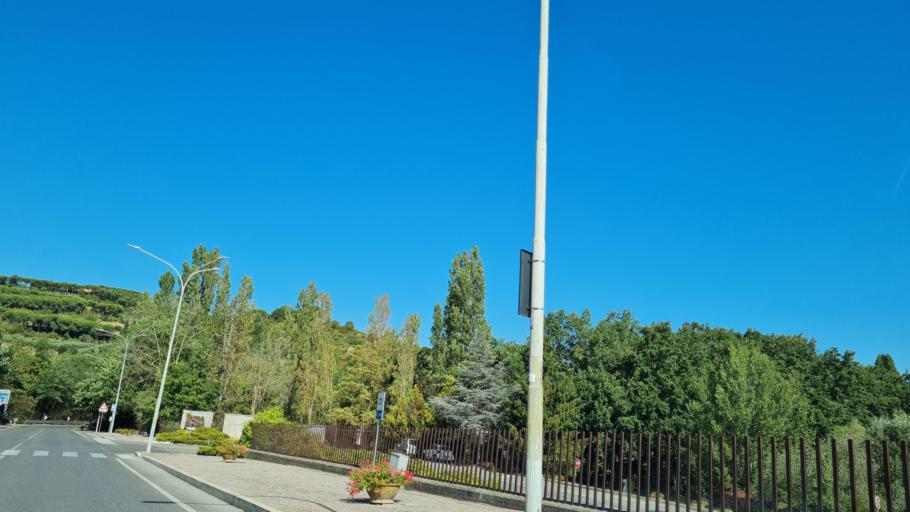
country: IT
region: Tuscany
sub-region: Provincia di Siena
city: Sant'Albino
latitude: 43.0728
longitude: 11.8020
